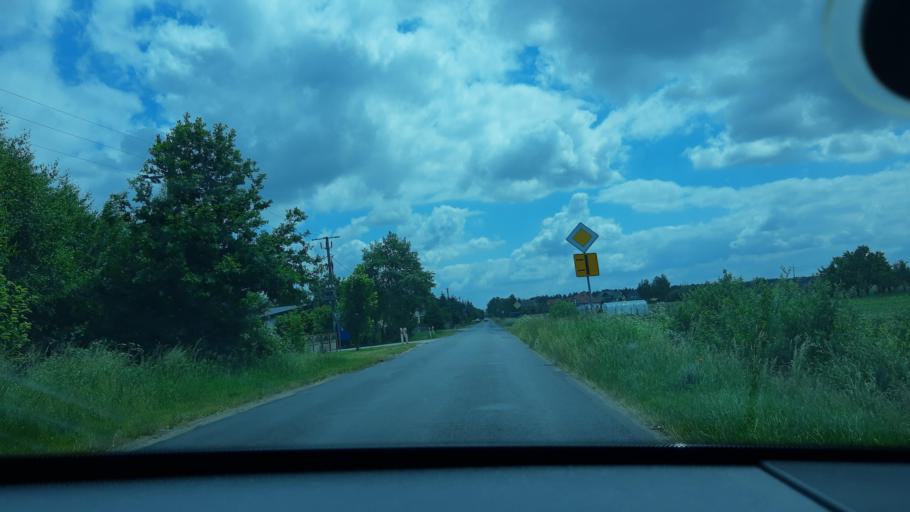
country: PL
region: Lodz Voivodeship
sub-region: Powiat sieradzki
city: Sieradz
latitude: 51.5414
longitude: 18.7969
